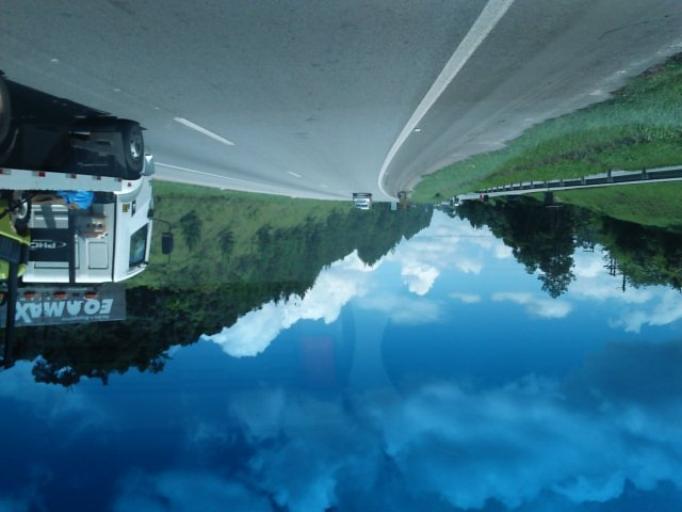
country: BR
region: Sao Paulo
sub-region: Juquitiba
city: Juquitiba
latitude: -23.9441
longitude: -47.0969
